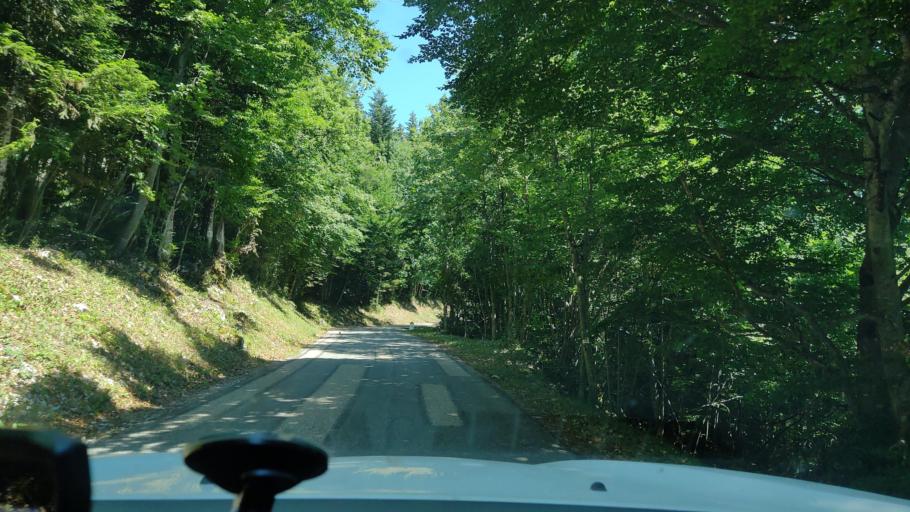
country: FR
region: Rhone-Alpes
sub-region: Departement de la Savoie
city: Le Bourget-du-Lac
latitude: 45.6603
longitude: 5.8365
